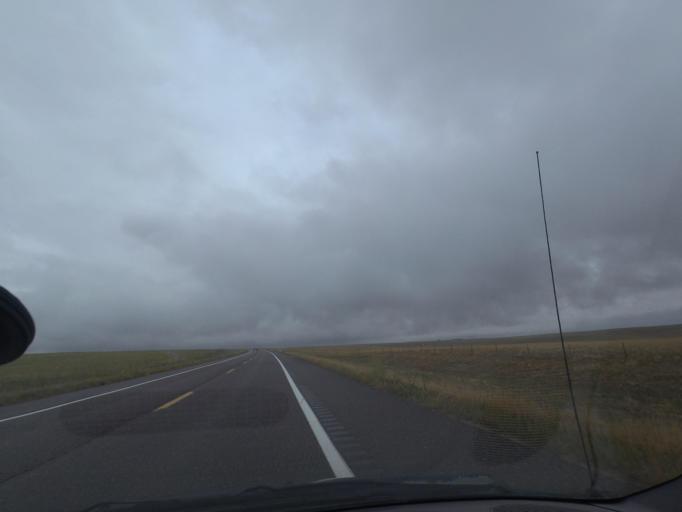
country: US
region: Colorado
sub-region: Arapahoe County
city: Byers
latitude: 39.7332
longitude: -103.9566
